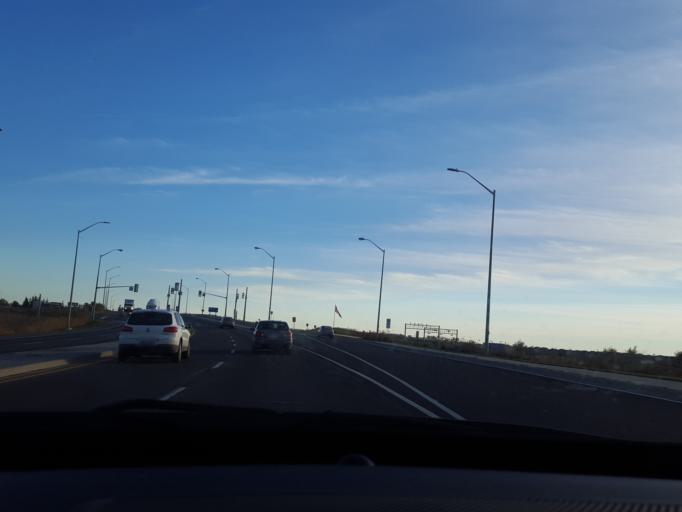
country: CA
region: Ontario
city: Markham
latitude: 43.8774
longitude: -79.2142
